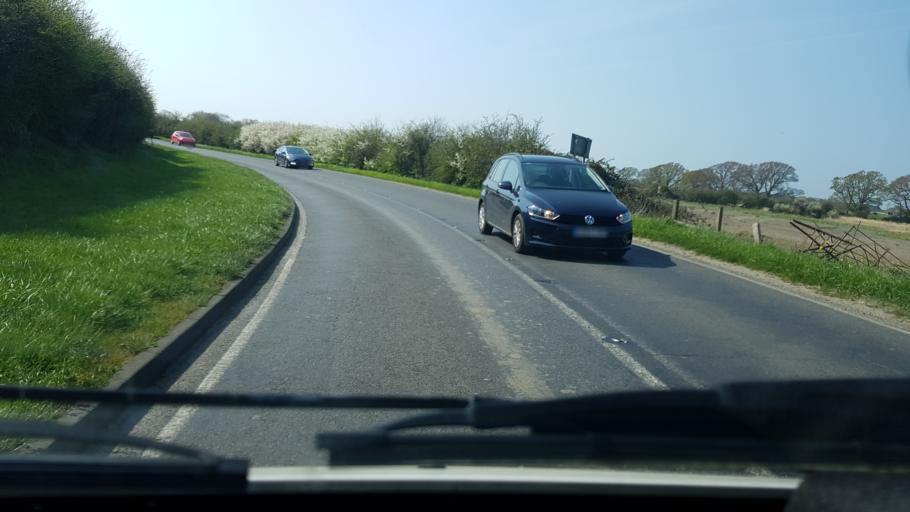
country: GB
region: England
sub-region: West Sussex
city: Birdham
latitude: 50.8079
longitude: -0.8038
